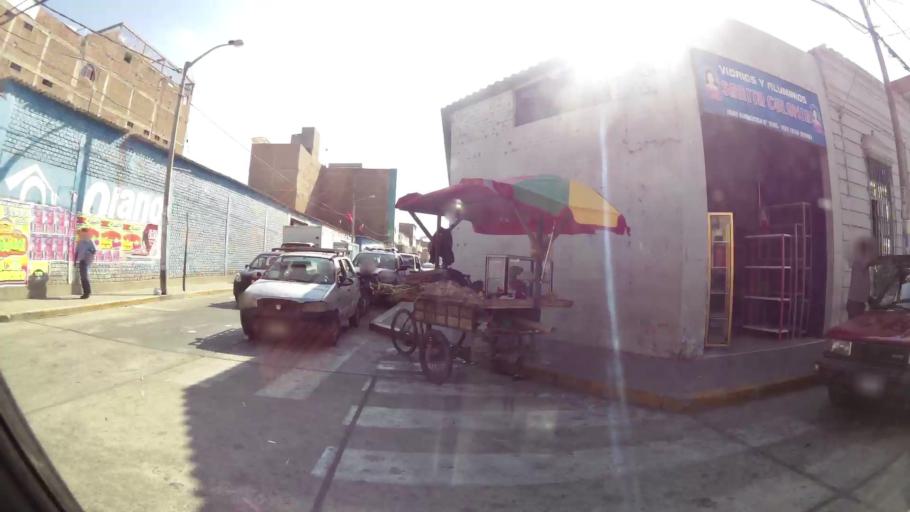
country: PE
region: Lambayeque
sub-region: Provincia de Chiclayo
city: Chiclayo
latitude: -6.7690
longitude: -79.8403
